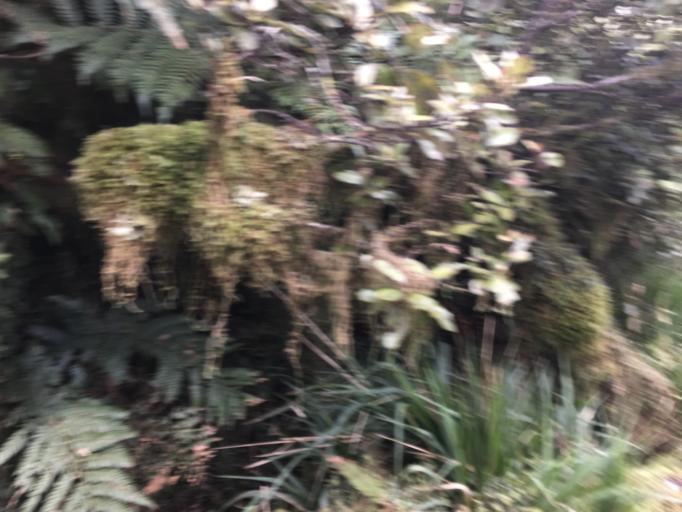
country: NZ
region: Manawatu-Wanganui
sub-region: Palmerston North City
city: Palmerston North
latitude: -40.4845
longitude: 175.6357
